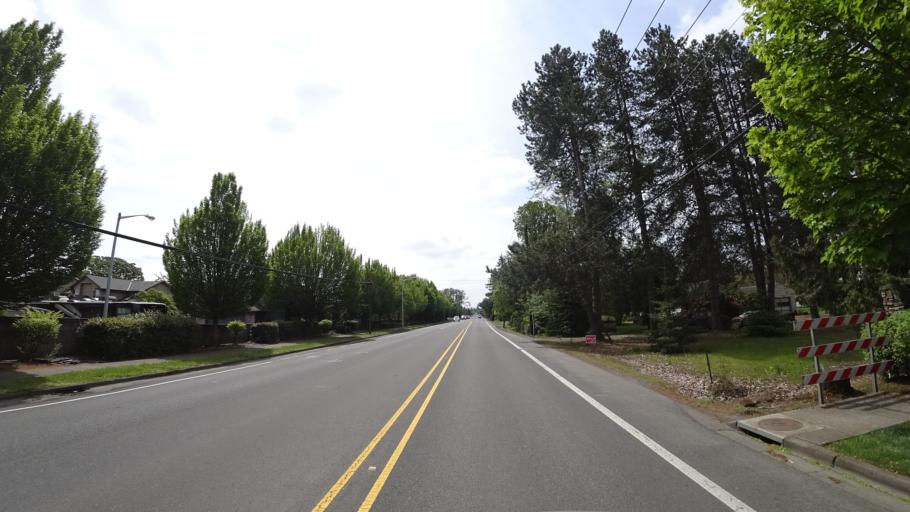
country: US
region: Oregon
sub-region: Washington County
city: Hillsboro
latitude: 45.5461
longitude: -122.9957
